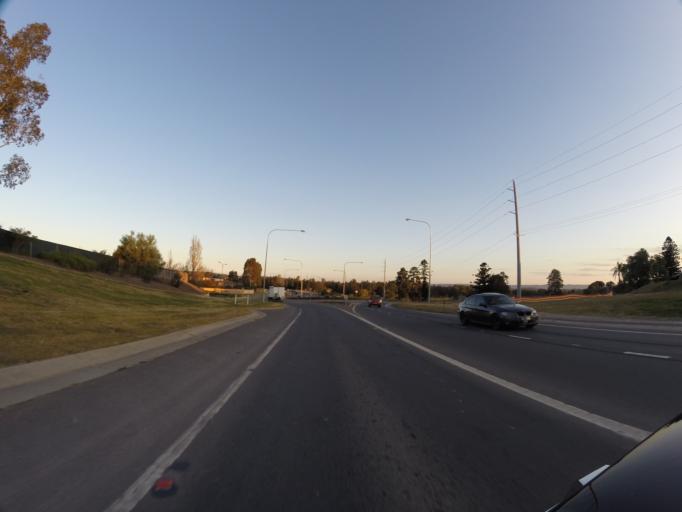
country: AU
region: New South Wales
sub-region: Camden
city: Narellan
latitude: -34.0251
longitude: 150.7265
